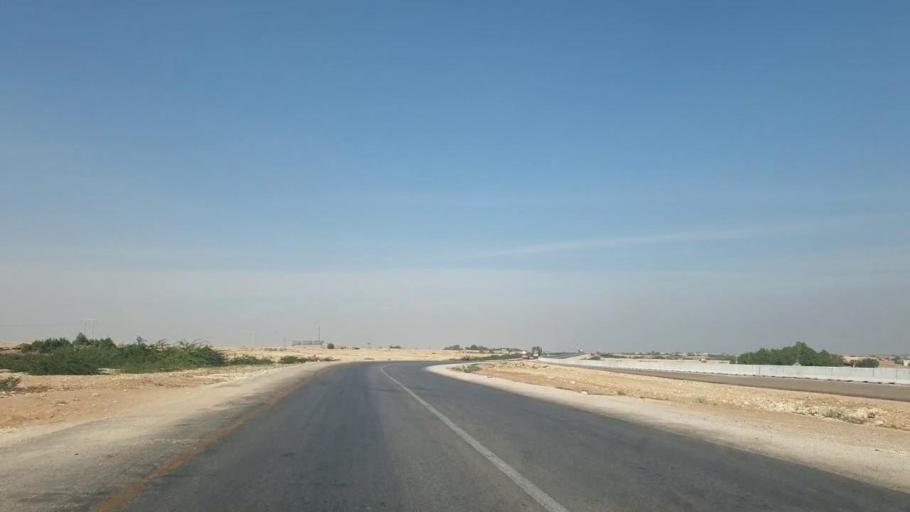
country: PK
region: Sindh
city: Matiari
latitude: 25.6843
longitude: 68.2956
